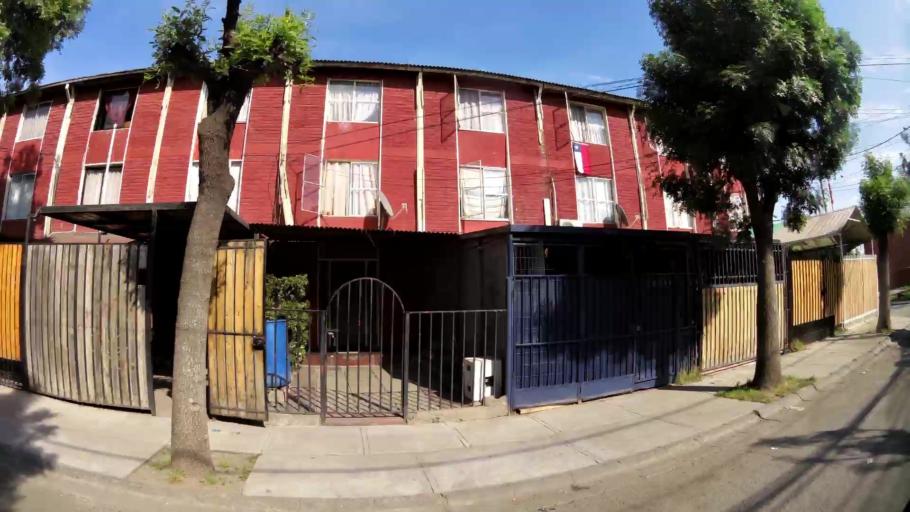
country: CL
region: Santiago Metropolitan
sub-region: Provincia de Cordillera
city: Puente Alto
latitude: -33.5683
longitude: -70.5855
